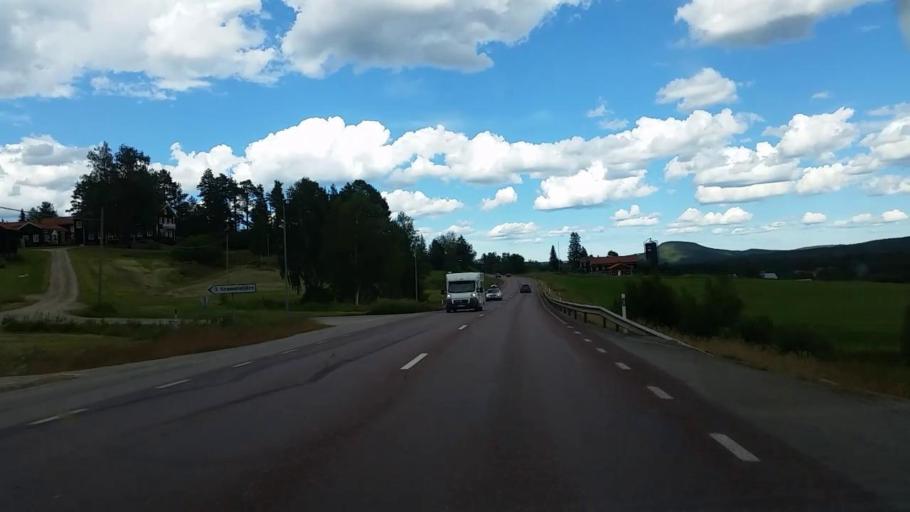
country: SE
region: Gaevleborg
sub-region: Ljusdals Kommun
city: Jaervsoe
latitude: 61.6953
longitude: 16.1574
